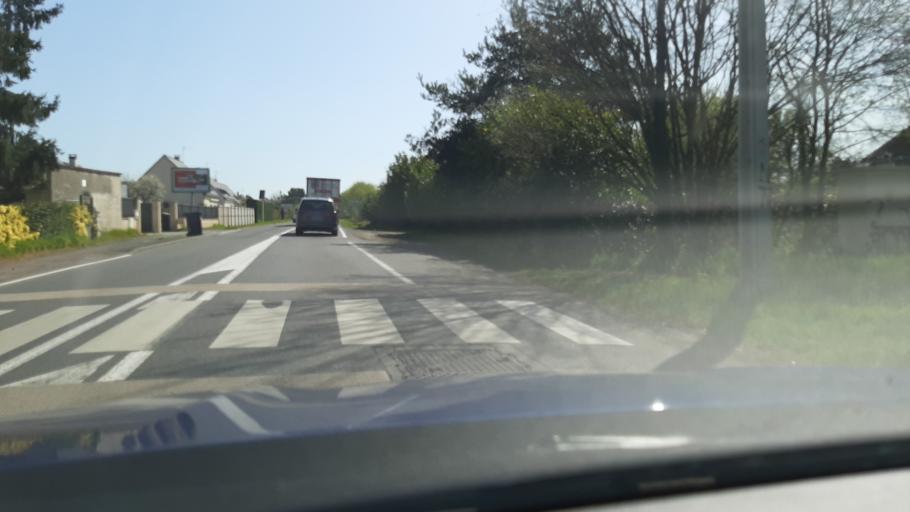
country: FR
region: Pays de la Loire
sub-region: Departement de Maine-et-Loire
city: Pellouailles-les-Vignes
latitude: 47.5178
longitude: -0.4826
